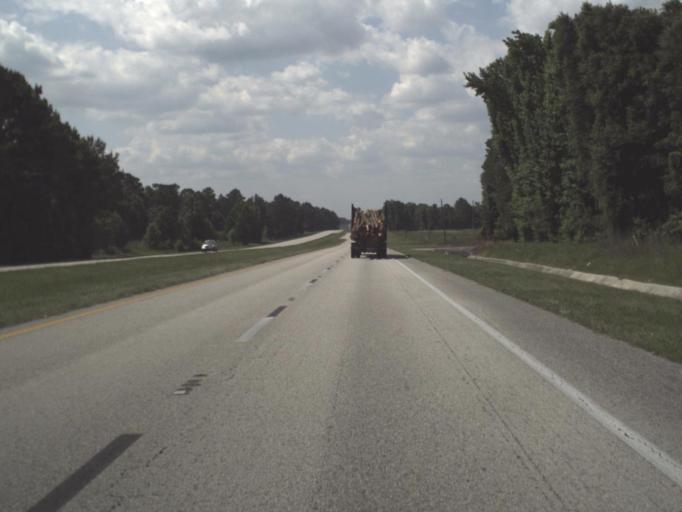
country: US
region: Florida
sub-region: Alachua County
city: Hawthorne
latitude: 29.6724
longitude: -82.1202
